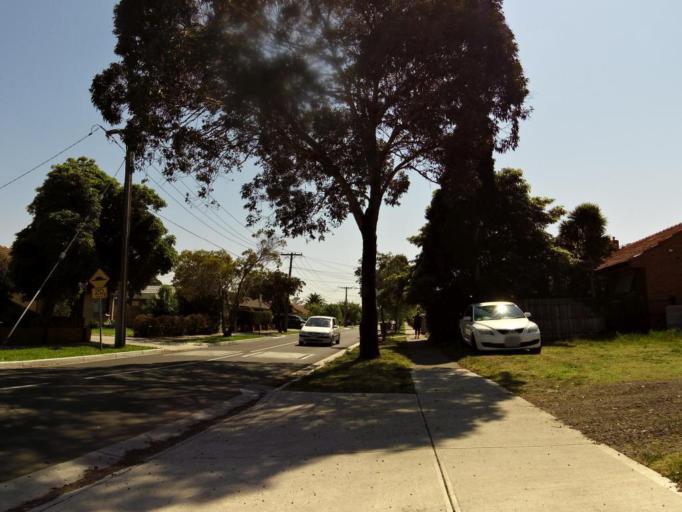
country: AU
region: Victoria
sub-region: Hume
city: Jacana
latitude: -37.6934
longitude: 144.9142
